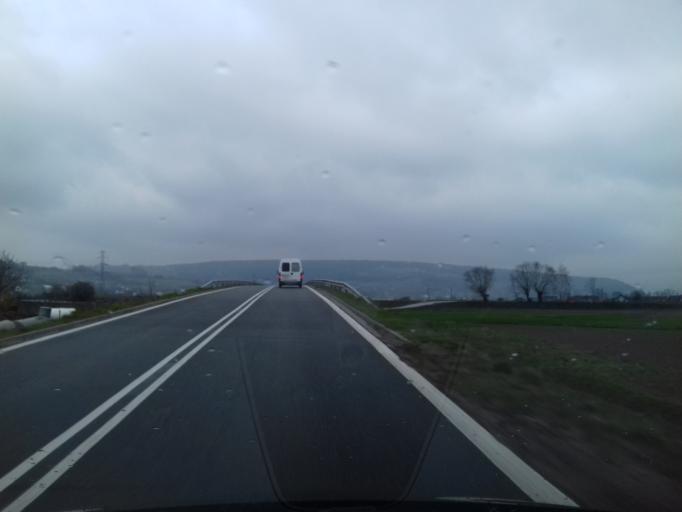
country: PL
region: Lesser Poland Voivodeship
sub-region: Powiat nowosadecki
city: Chelmiec
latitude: 49.6143
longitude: 20.6407
